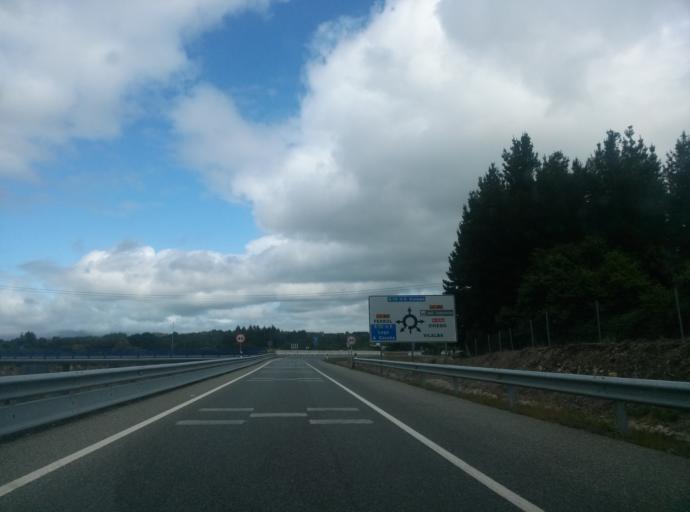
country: ES
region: Galicia
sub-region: Provincia de Lugo
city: Vilalba
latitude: 43.3173
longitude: -7.6959
